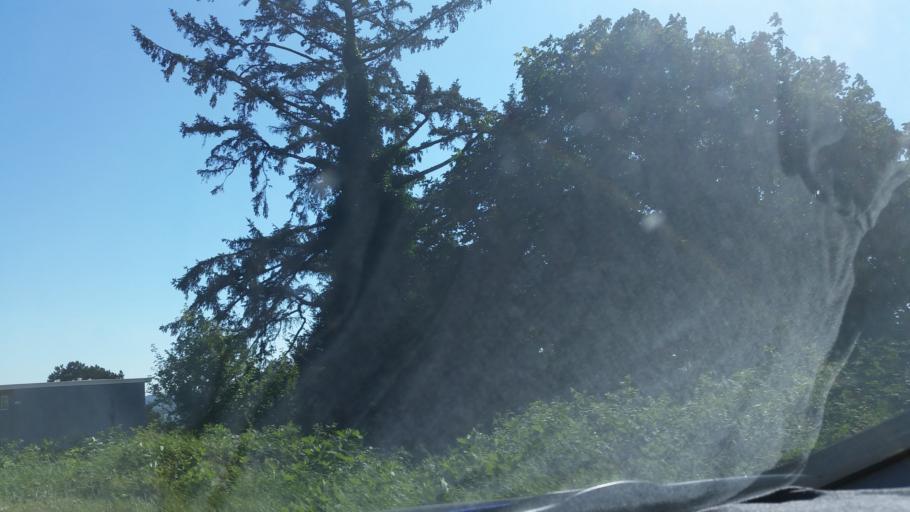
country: US
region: Oregon
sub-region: Clatsop County
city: Astoria
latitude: 46.1826
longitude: -123.8582
